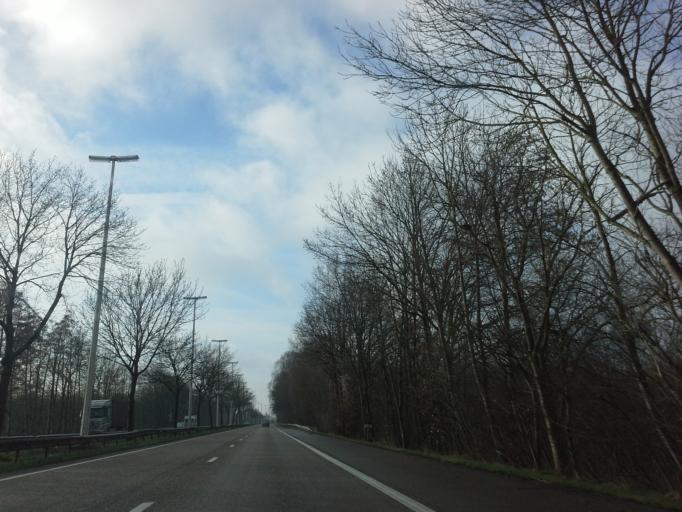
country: BE
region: Flanders
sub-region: Provincie Limburg
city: Nieuwerkerken
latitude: 50.8341
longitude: 5.2338
